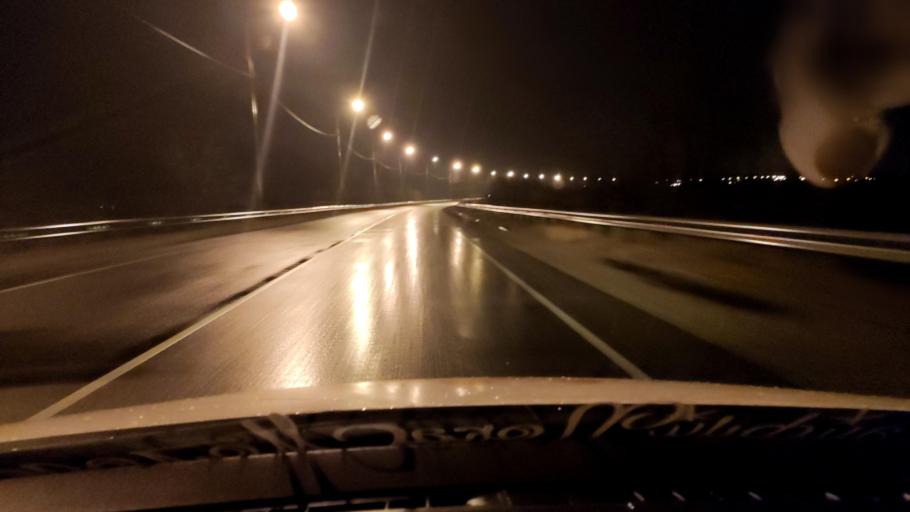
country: RU
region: Voronezj
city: Pridonskoy
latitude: 51.7189
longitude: 39.0726
